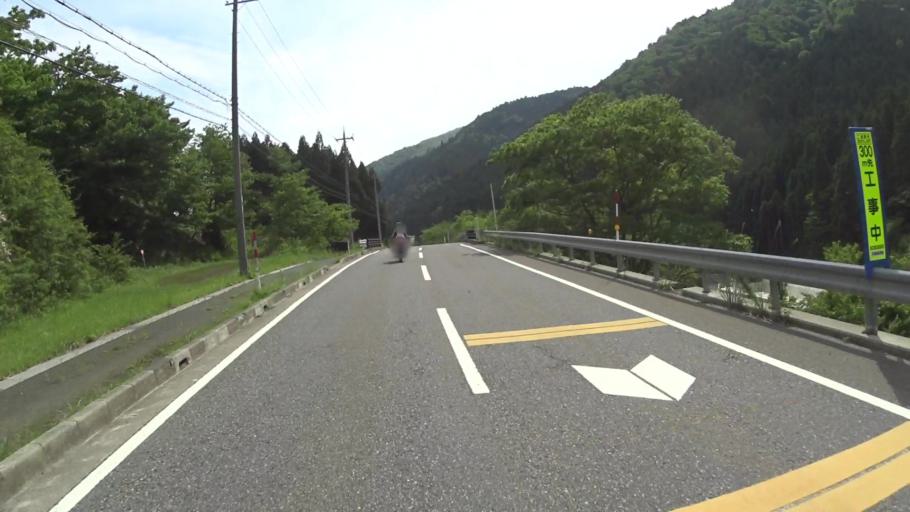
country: JP
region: Shiga Prefecture
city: Kitahama
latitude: 35.2589
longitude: 135.8721
